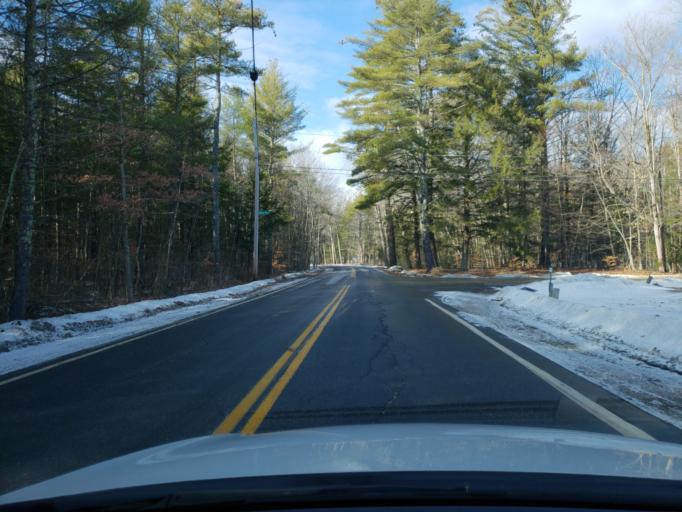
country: US
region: New Hampshire
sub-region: Hillsborough County
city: New Boston
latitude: 42.9991
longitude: -71.7573
